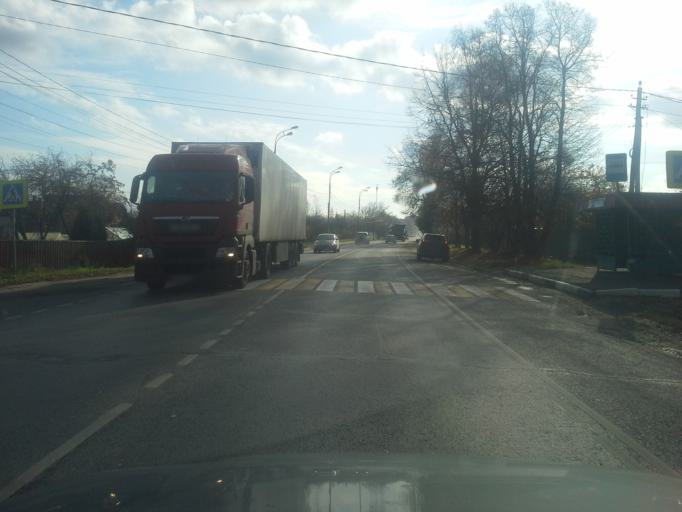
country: RU
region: Moskovskaya
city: Zvenigorod
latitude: 55.6951
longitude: 36.8897
